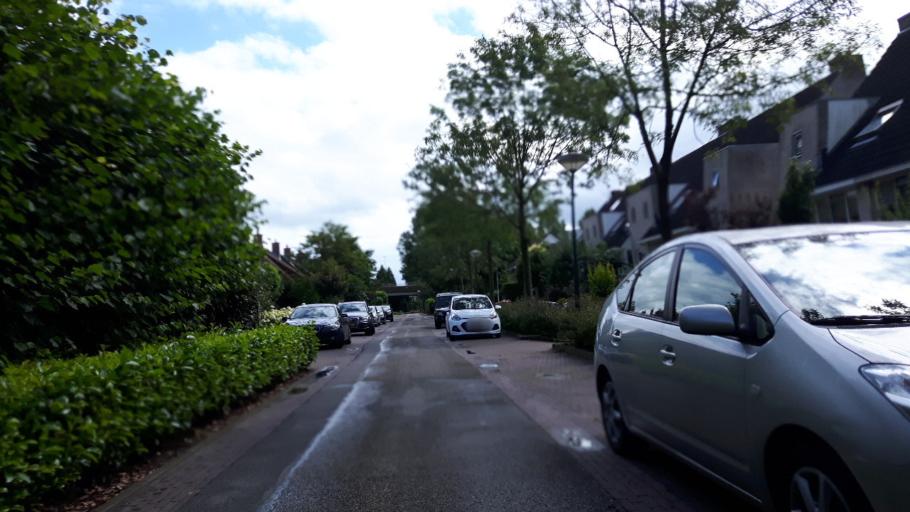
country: NL
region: Utrecht
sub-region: Gemeente IJsselstein
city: IJsselstein
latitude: 52.0280
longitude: 5.0371
